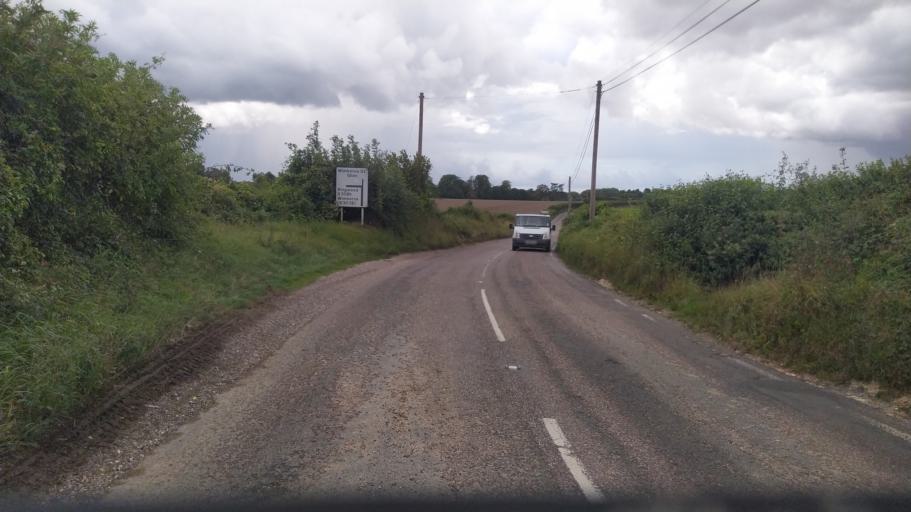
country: GB
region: England
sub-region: Dorset
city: Verwood
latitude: 50.9125
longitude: -1.9461
